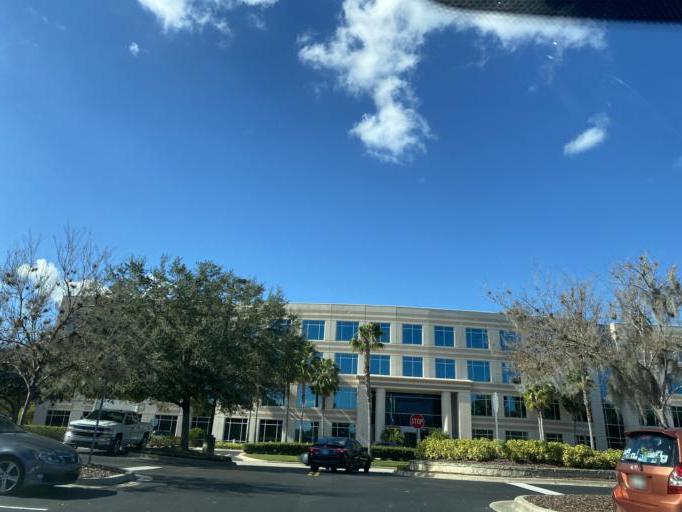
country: US
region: Florida
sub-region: Seminole County
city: Heathrow
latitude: 28.7908
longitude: -81.3538
